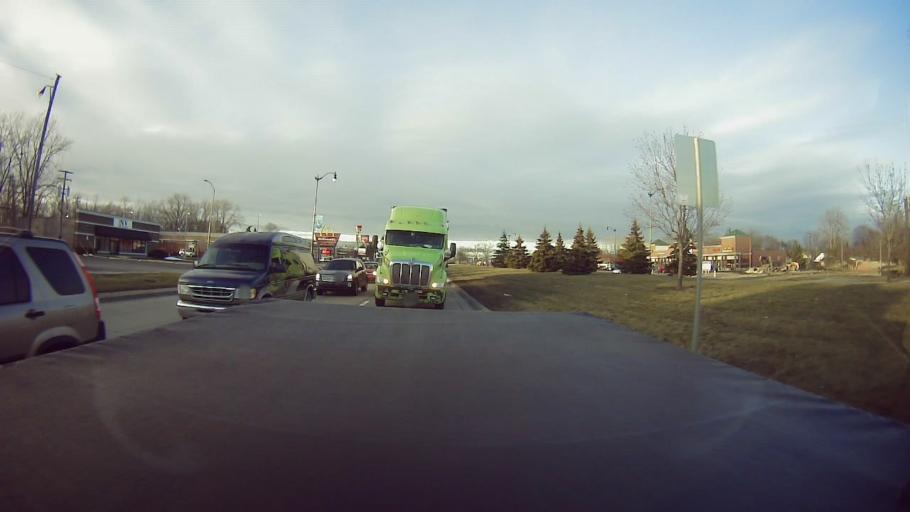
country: US
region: Michigan
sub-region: Wayne County
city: Taylor
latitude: 42.2313
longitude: -83.2695
